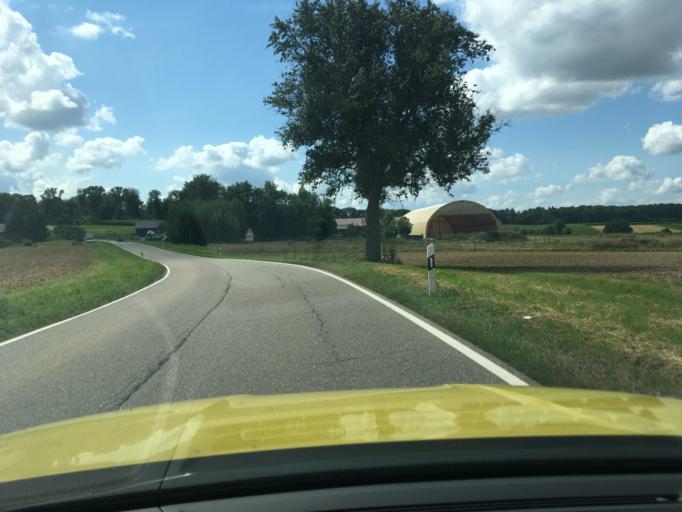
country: DE
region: Baden-Wuerttemberg
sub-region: Regierungsbezirk Stuttgart
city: Massenbachhausen
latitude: 49.2012
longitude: 9.0514
